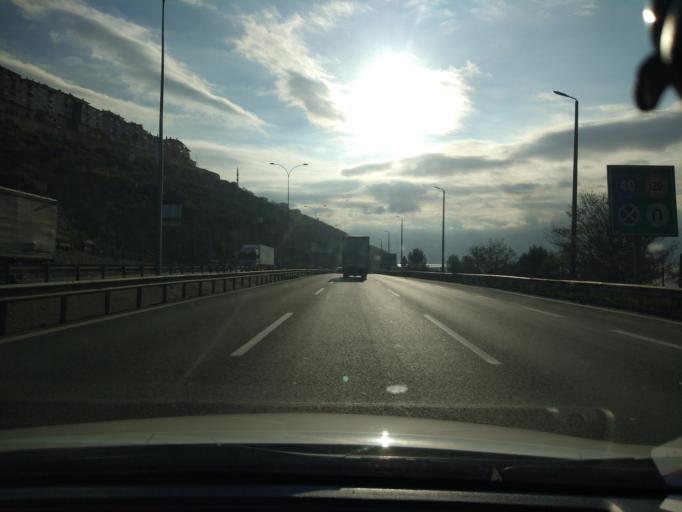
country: TR
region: Kocaeli
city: Hereke
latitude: 40.7861
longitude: 29.6228
